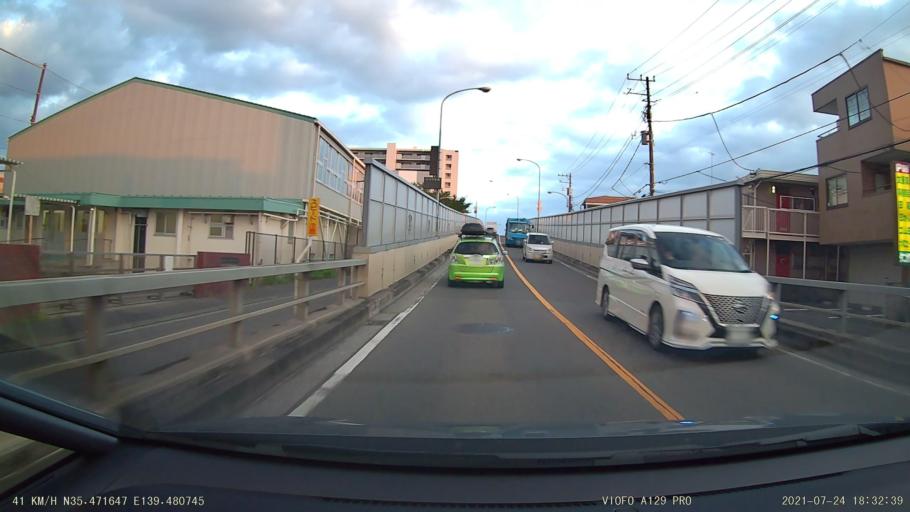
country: JP
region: Kanagawa
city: Minami-rinkan
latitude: 35.4716
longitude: 139.4809
